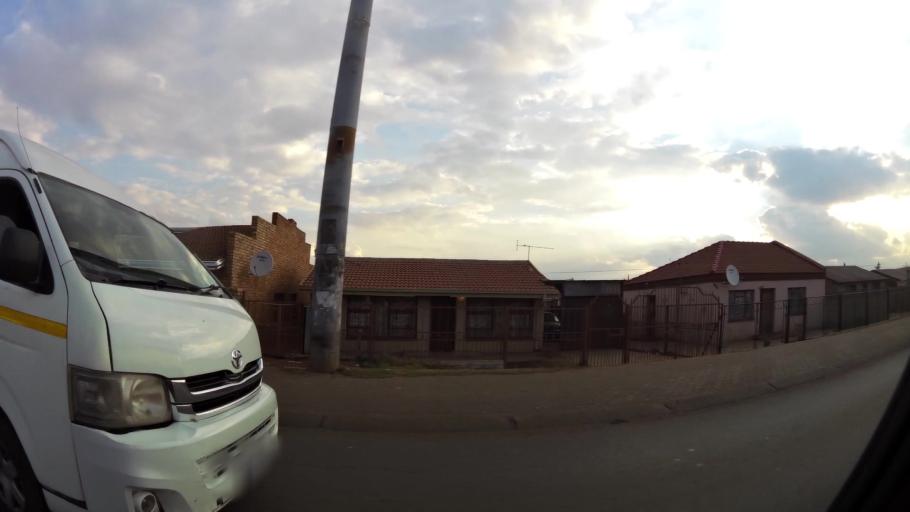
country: ZA
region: Gauteng
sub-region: City of Johannesburg Metropolitan Municipality
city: Orange Farm
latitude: -26.5704
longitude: 27.8373
